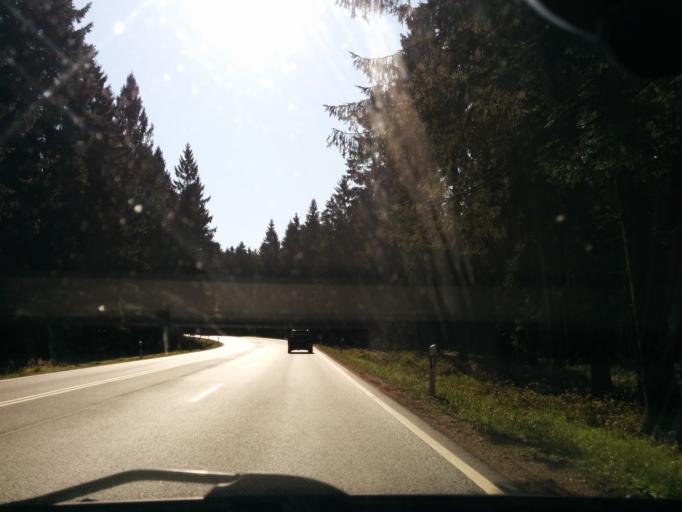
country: DE
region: Lower Saxony
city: Altenau
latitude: 51.7742
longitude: 10.4244
